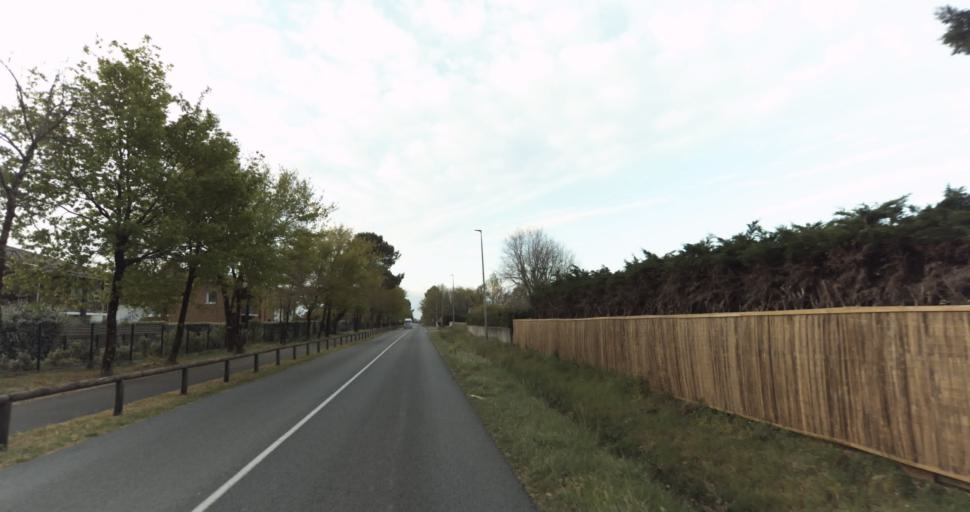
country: FR
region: Aquitaine
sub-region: Departement de la Gironde
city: Martignas-sur-Jalle
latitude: 44.8048
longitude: -0.7790
